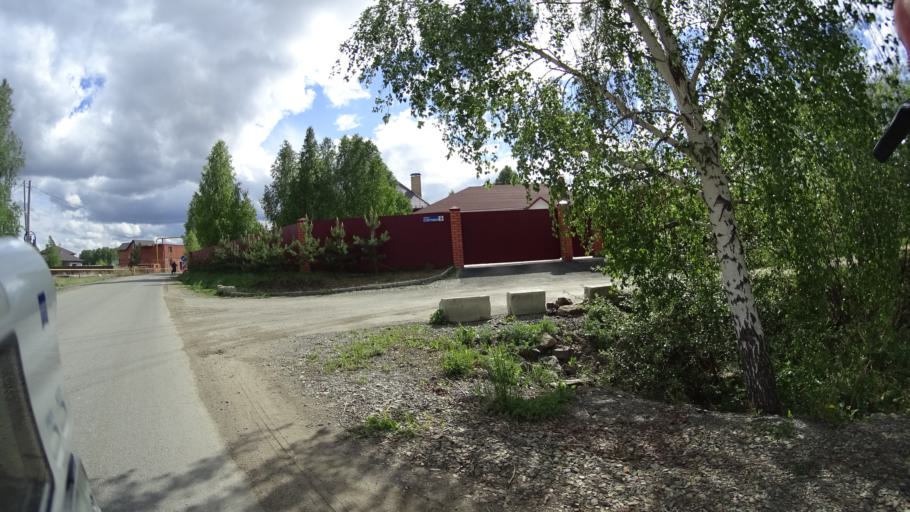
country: RU
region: Chelyabinsk
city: Sargazy
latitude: 55.1555
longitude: 61.2413
